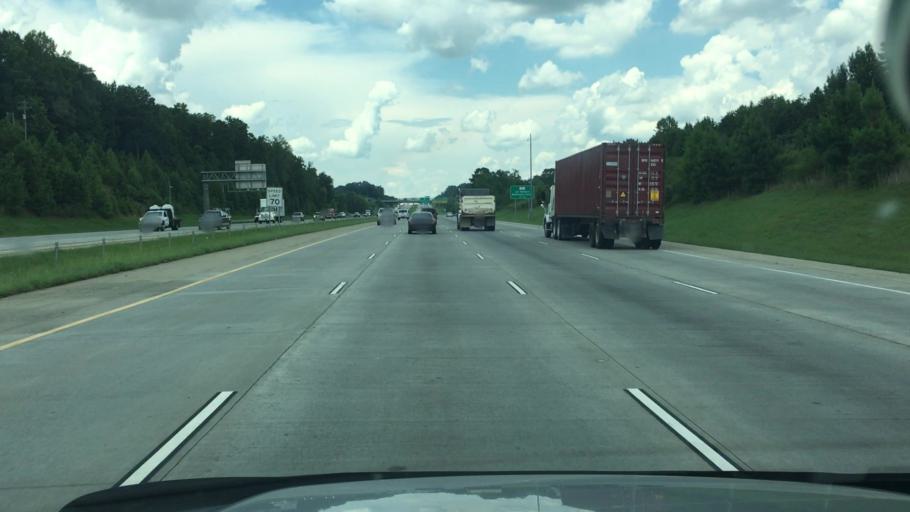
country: US
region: North Carolina
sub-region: Gaston County
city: Mount Holly
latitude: 35.2647
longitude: -80.9671
